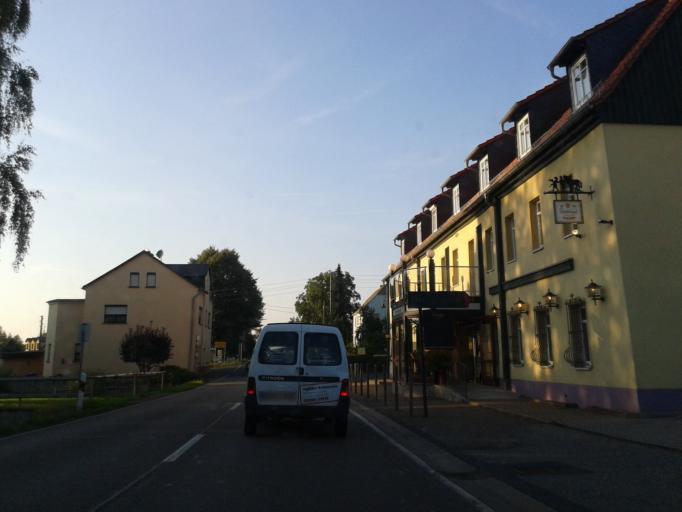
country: DE
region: Saxony
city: Klipphausen
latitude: 51.0769
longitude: 13.5066
